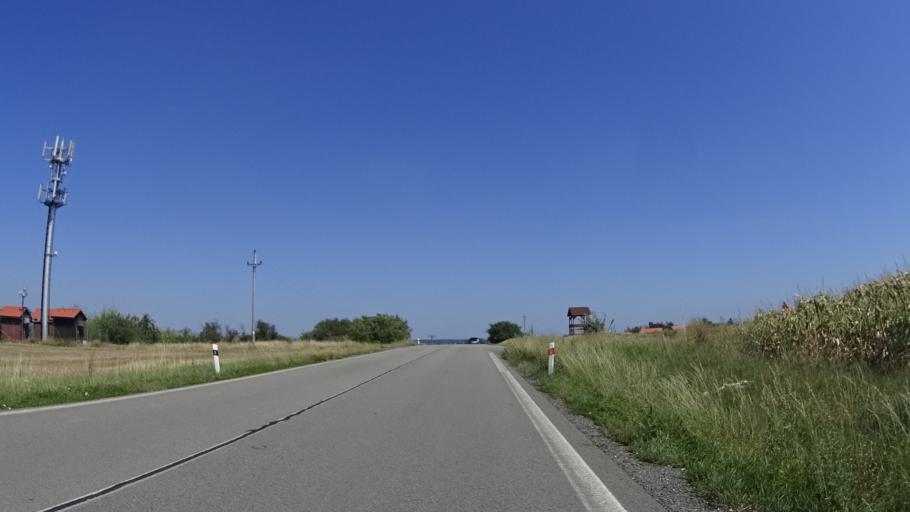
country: CZ
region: South Moravian
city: Sudomerice
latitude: 48.8760
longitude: 17.2659
